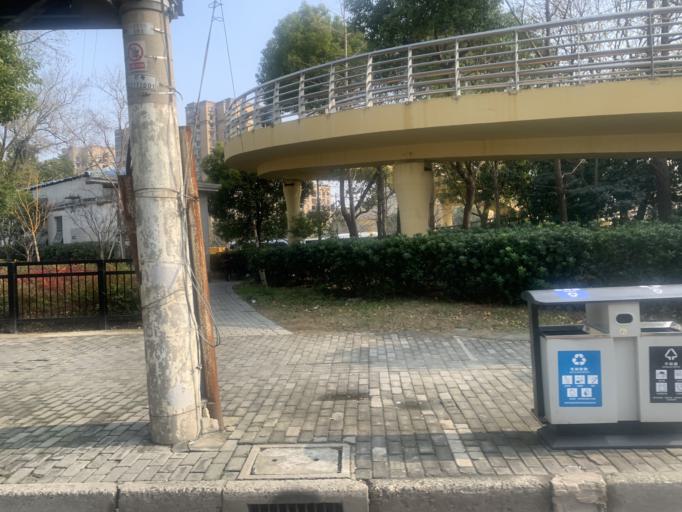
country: CN
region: Shanghai Shi
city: Huamu
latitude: 31.1822
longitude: 121.5158
